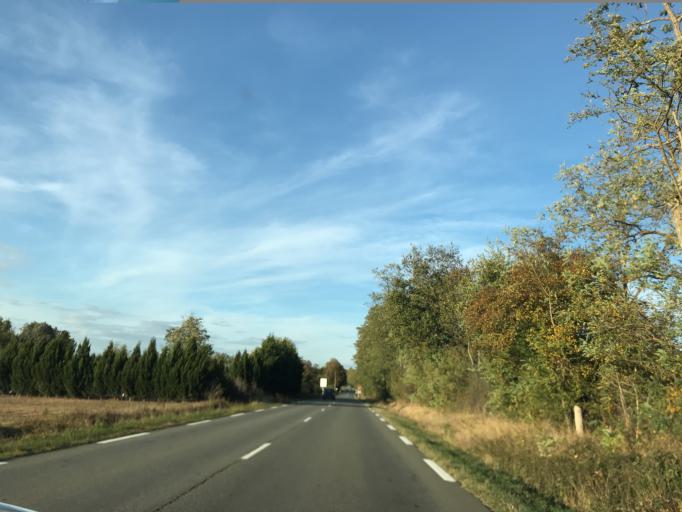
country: FR
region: Auvergne
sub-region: Departement du Puy-de-Dome
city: Puy-Guillaume
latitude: 45.9802
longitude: 3.4836
